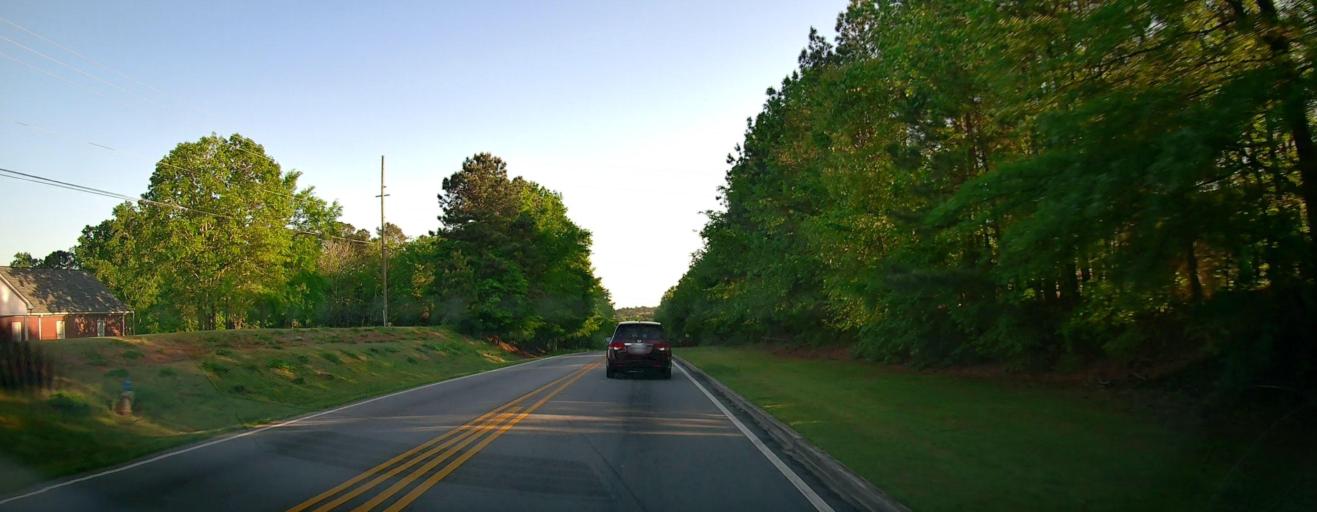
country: US
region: Georgia
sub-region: Newton County
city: Covington
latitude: 33.5853
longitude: -83.8343
